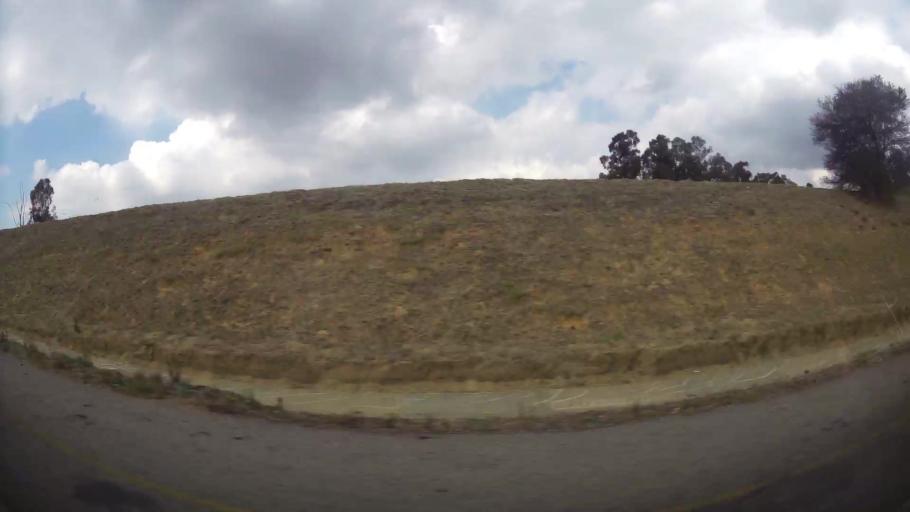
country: ZA
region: Gauteng
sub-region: Sedibeng District Municipality
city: Vereeniging
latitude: -26.6970
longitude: 27.9365
